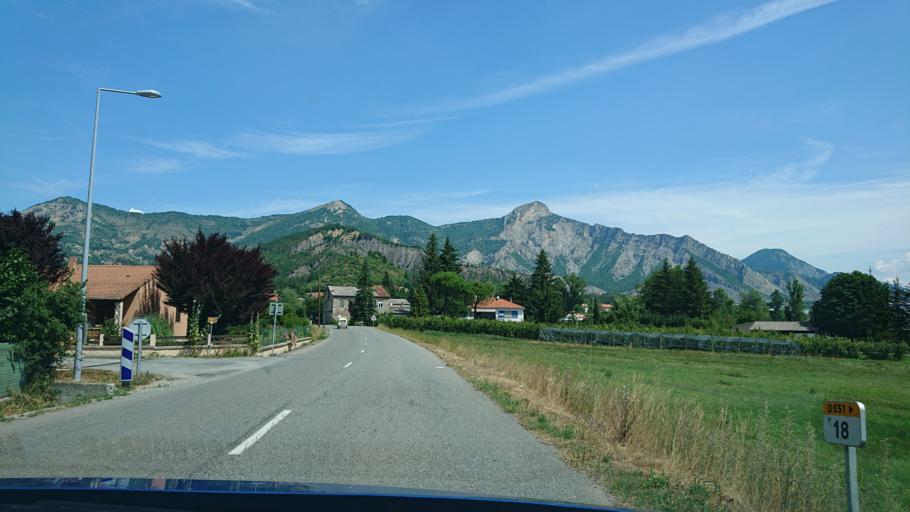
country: FR
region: Provence-Alpes-Cote d'Azur
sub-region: Departement des Hautes-Alpes
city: Tallard
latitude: 44.3392
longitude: 6.0282
